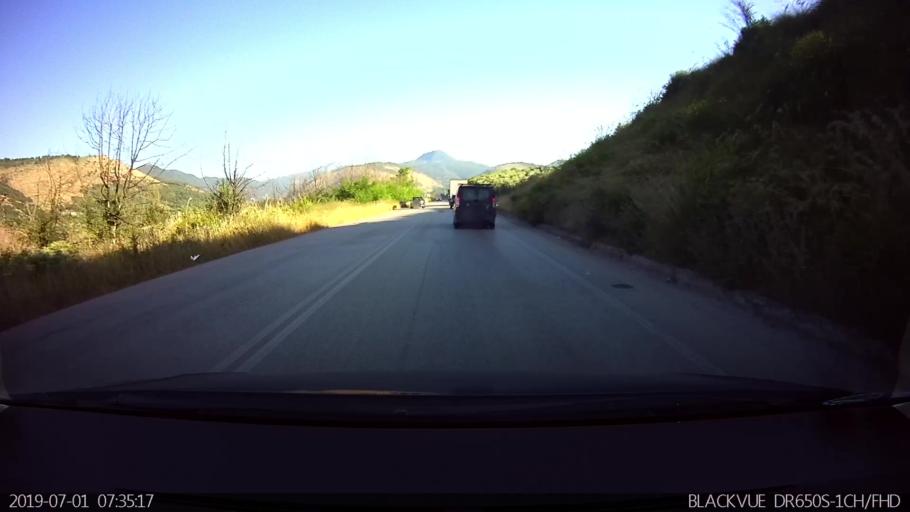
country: IT
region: Latium
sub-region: Provincia di Latina
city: Prossedi
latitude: 41.5235
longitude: 13.2708
